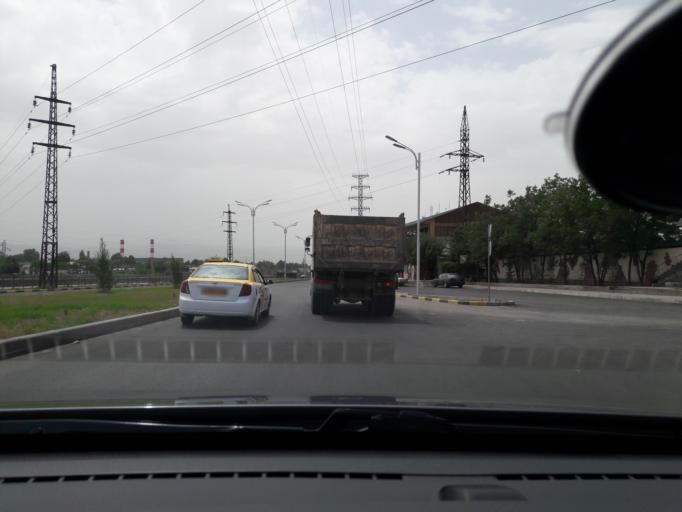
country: TJ
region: Dushanbe
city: Dushanbe
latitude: 38.5638
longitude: 68.7688
